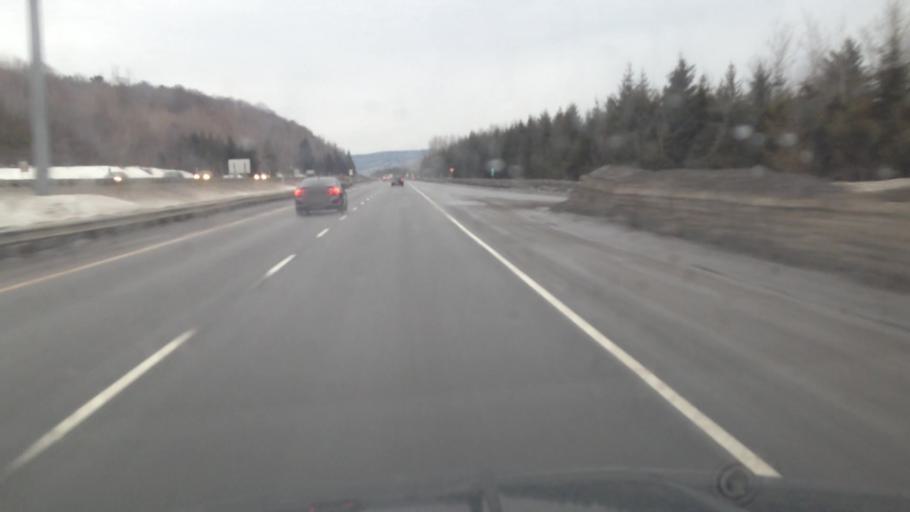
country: CA
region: Quebec
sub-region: Laurentides
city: Prevost
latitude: 45.8443
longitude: -74.0697
